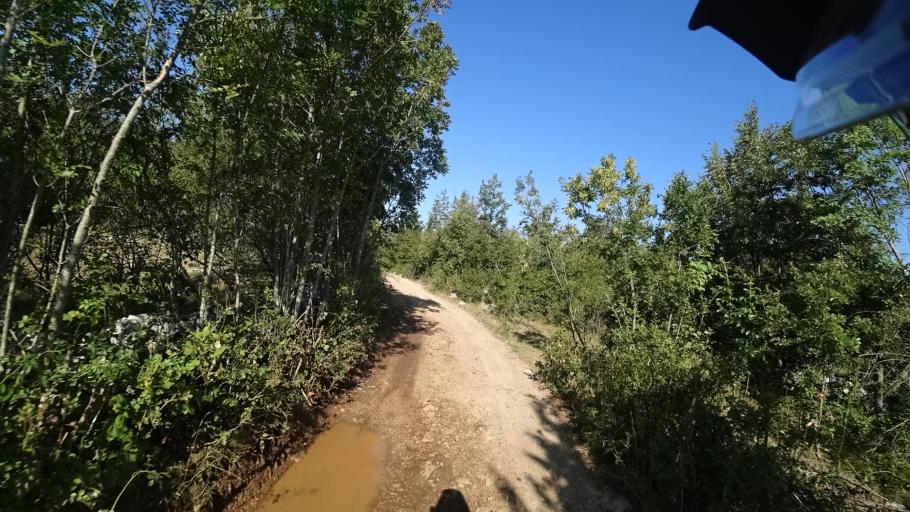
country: HR
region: Sibensko-Kniniska
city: Knin
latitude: 44.2246
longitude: 16.0990
